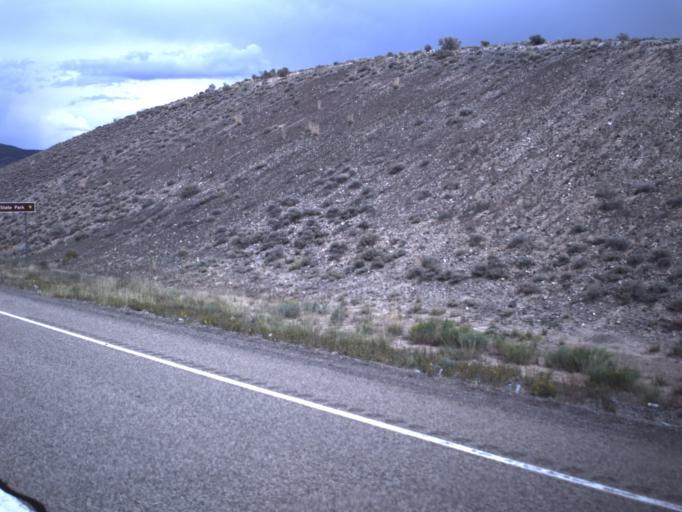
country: US
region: Utah
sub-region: Piute County
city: Junction
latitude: 38.2122
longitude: -112.2236
